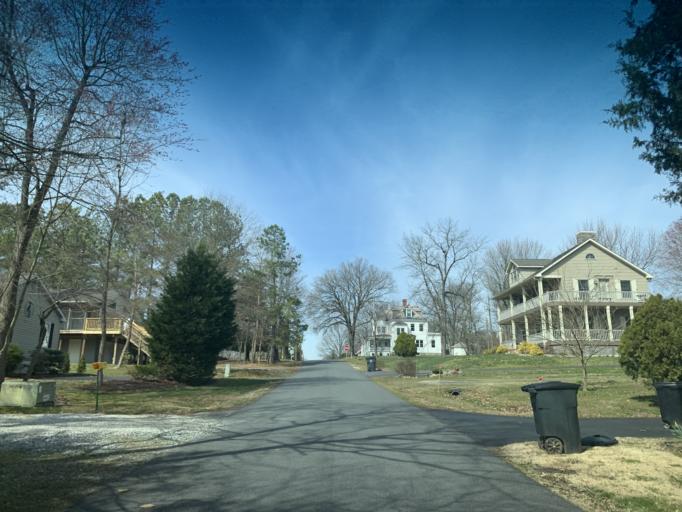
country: US
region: Maryland
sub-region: Cecil County
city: Charlestown
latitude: 39.5743
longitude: -75.9716
